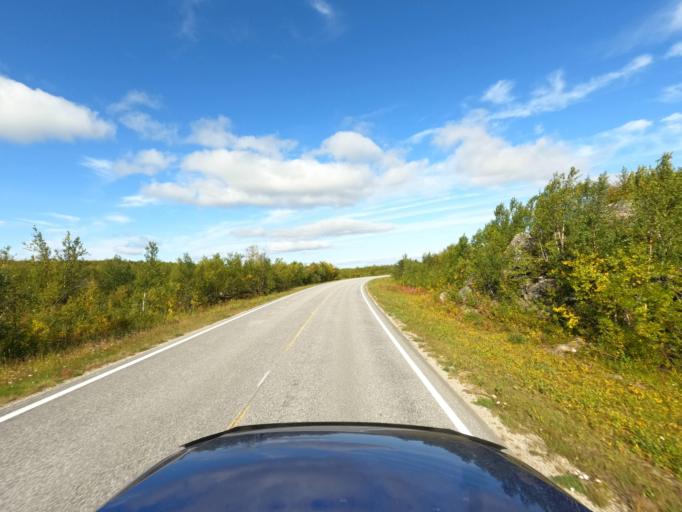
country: NO
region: Finnmark Fylke
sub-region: Karasjok
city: Karasjohka
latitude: 69.5956
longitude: 25.3302
